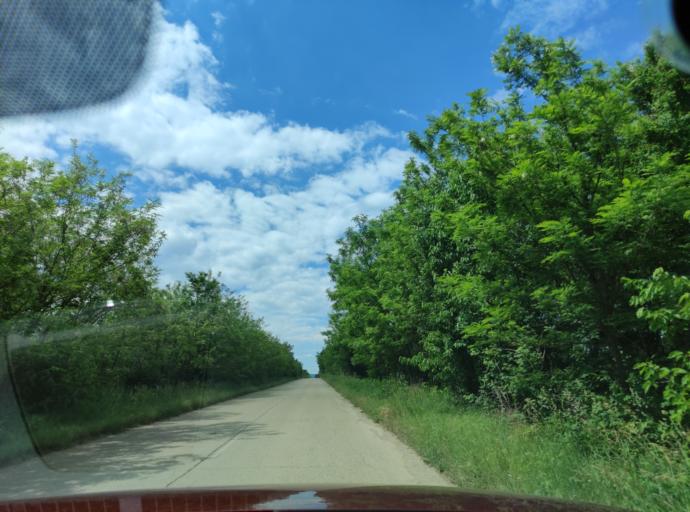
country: BG
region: Montana
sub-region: Obshtina Berkovitsa
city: Berkovitsa
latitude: 43.3643
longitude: 23.0874
